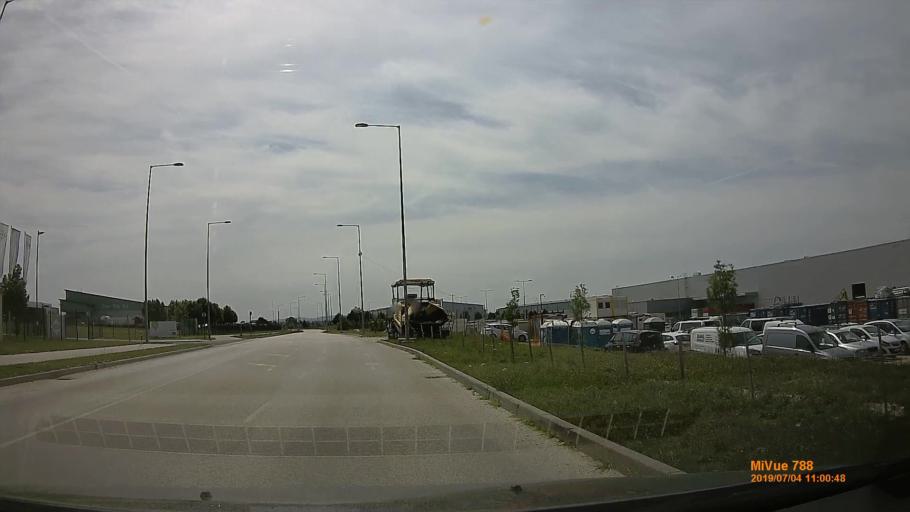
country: HU
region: Komarom-Esztergom
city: Tata
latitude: 47.6327
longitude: 18.2939
